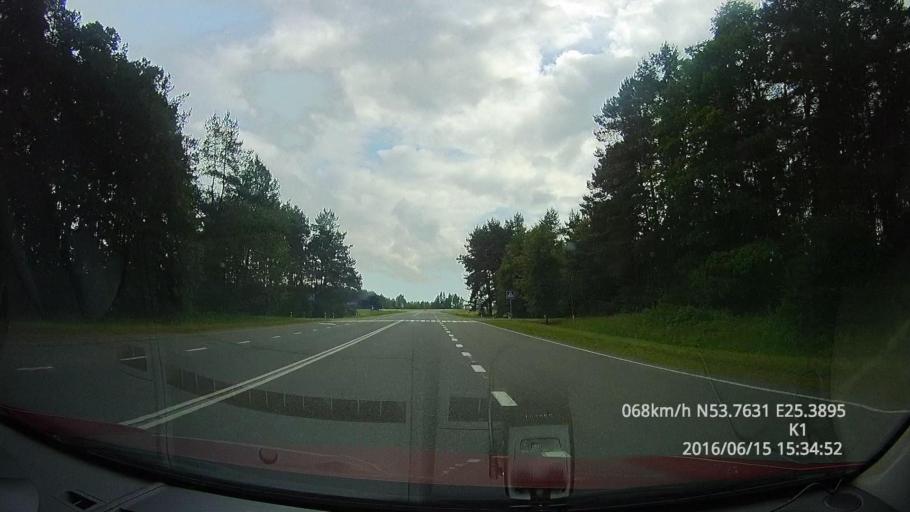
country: BY
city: Berezovka
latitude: 53.7625
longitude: 25.3898
